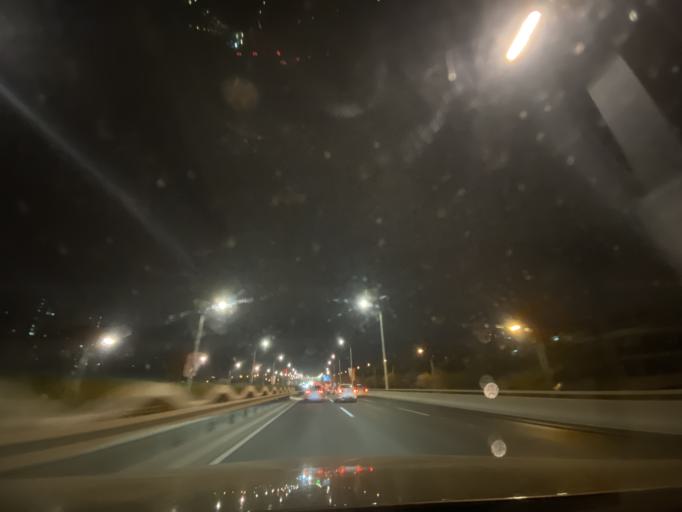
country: CN
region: Beijing
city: Lugu
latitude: 39.8958
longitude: 116.2227
